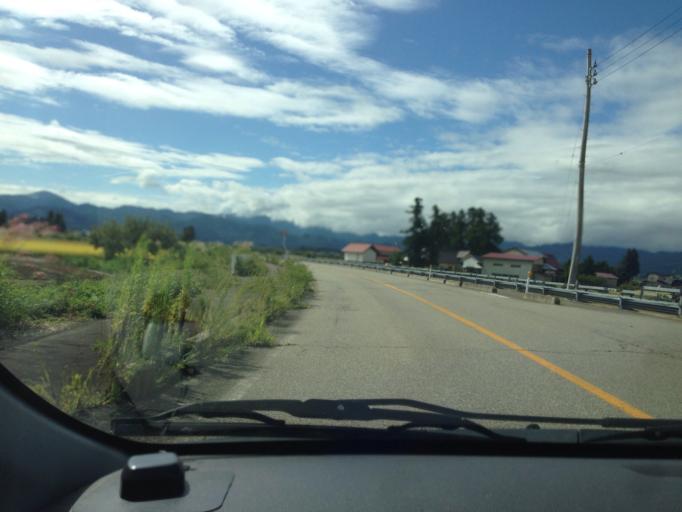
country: JP
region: Fukushima
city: Kitakata
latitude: 37.4851
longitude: 139.8489
